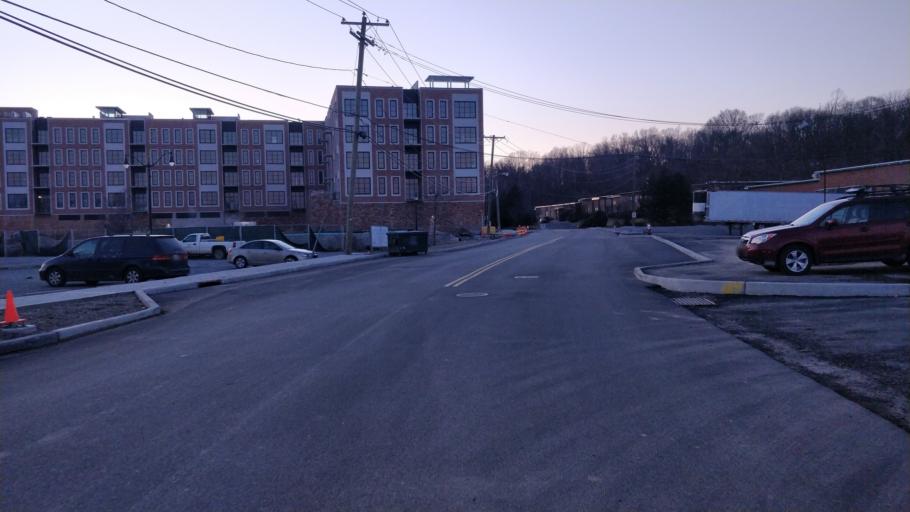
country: US
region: New York
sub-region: Nassau County
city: Sea Cliff
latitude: 40.8589
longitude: -73.6434
